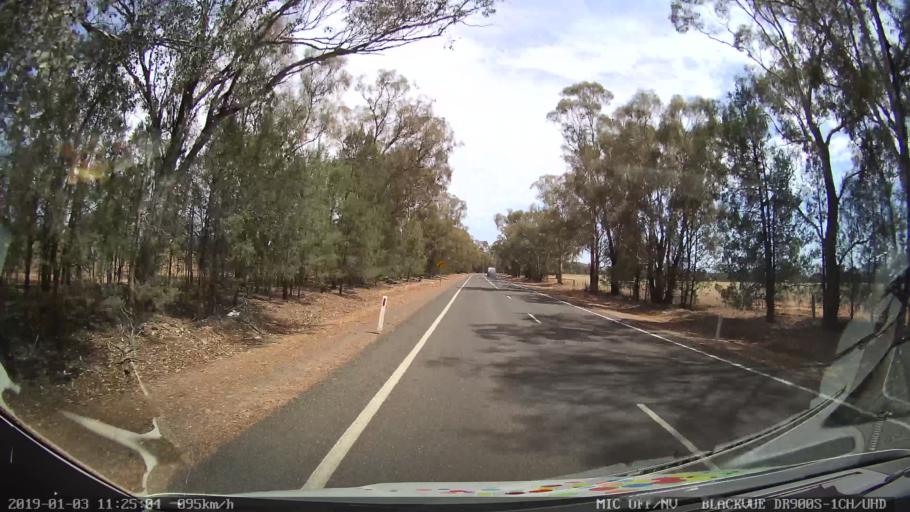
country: AU
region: New South Wales
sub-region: Weddin
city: Grenfell
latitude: -34.0435
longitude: 148.2307
